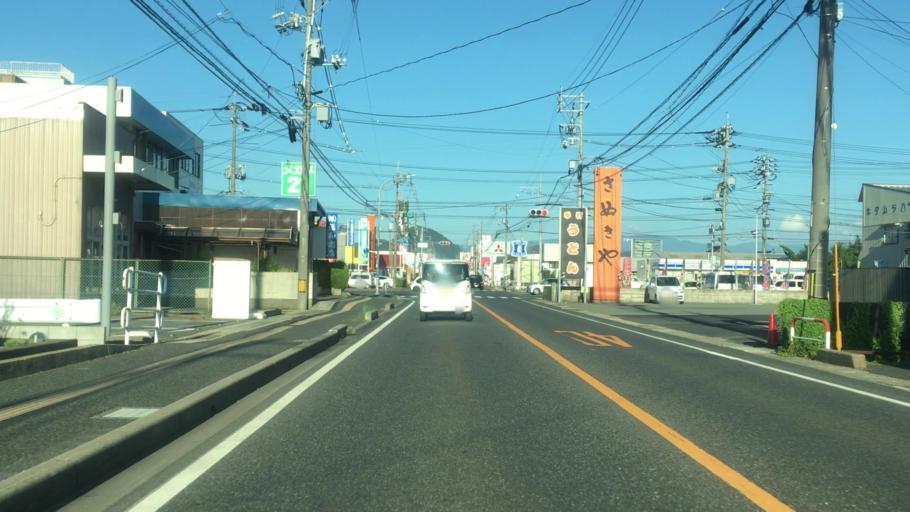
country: JP
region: Tottori
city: Tottori
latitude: 35.5146
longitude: 134.1911
